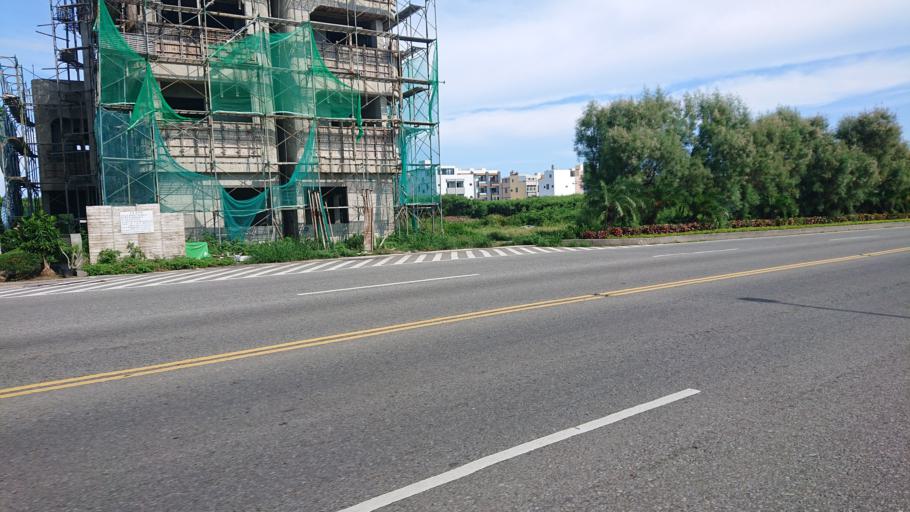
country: TW
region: Taiwan
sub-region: Penghu
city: Ma-kung
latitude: 23.5329
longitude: 119.6021
